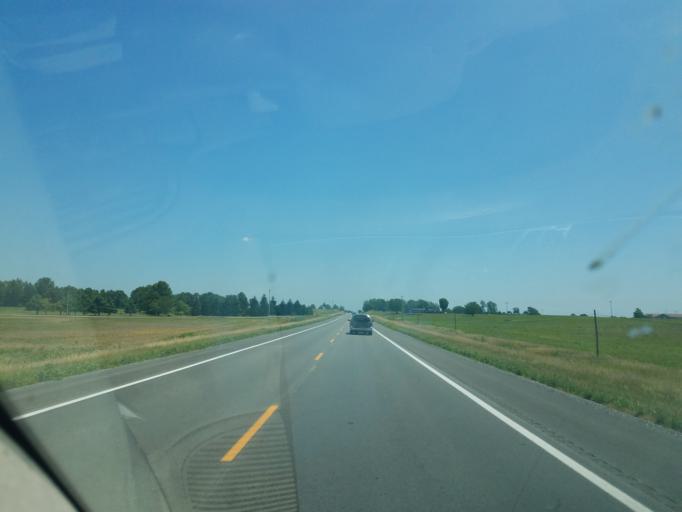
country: US
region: Ohio
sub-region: Hardin County
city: Ada
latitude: 40.7078
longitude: -83.7427
